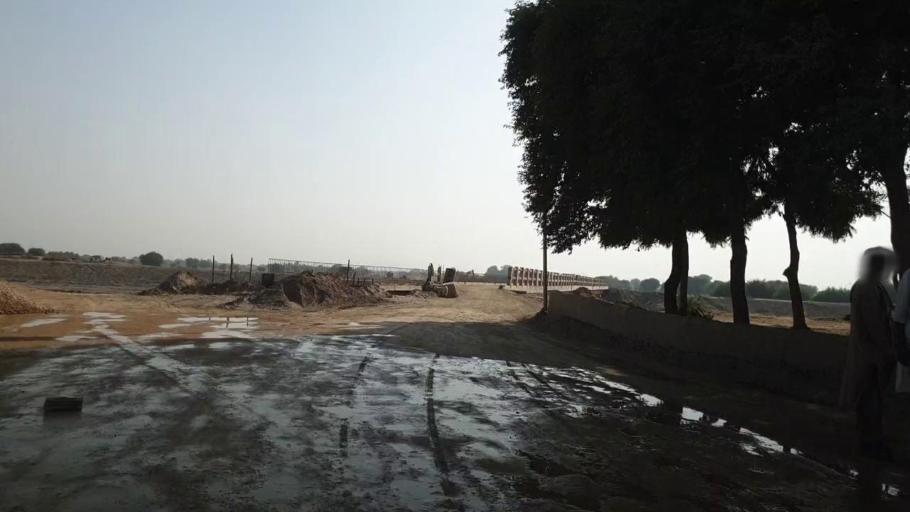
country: PK
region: Sindh
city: Bhan
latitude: 26.5014
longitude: 67.7822
